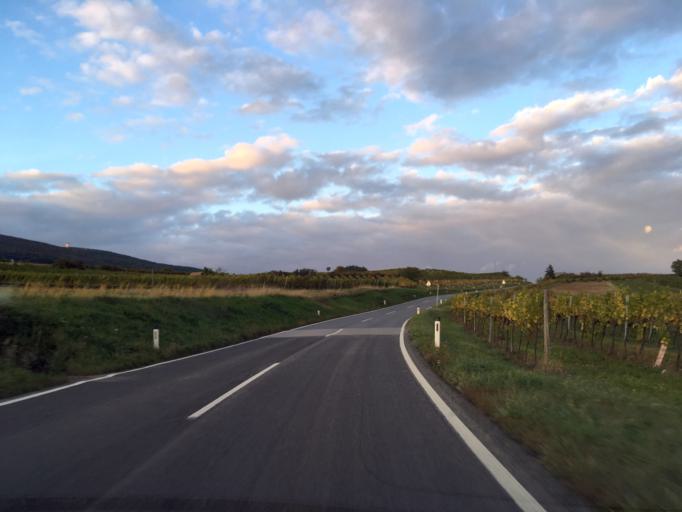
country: AT
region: Lower Austria
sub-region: Politischer Bezirk Baden
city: Pfaffstatten
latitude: 48.0249
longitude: 16.2590
